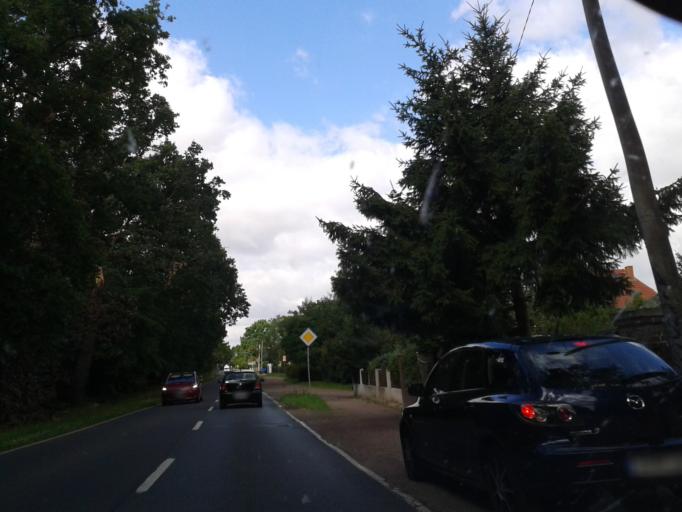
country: DE
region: Saxony-Anhalt
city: Halle Neustadt
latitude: 51.5108
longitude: 11.9136
